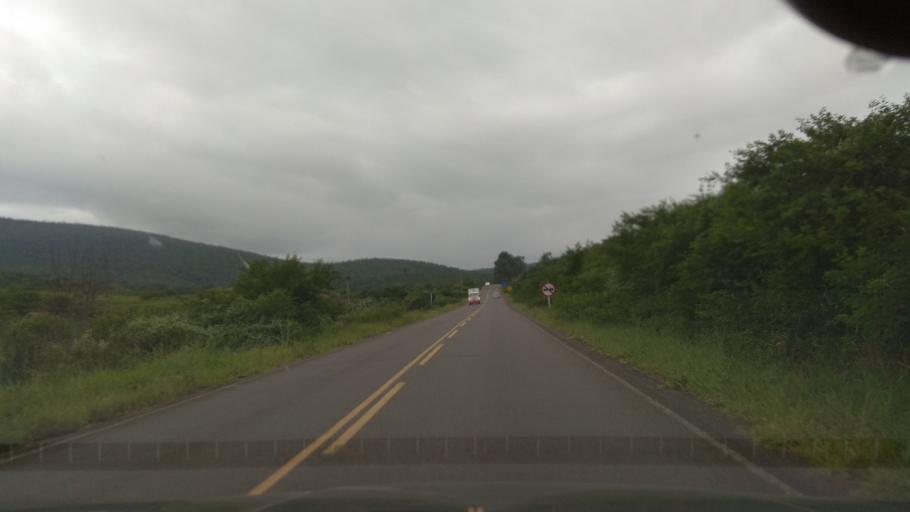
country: BR
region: Bahia
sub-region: Santa Ines
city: Santa Ines
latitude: -13.2751
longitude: -39.8096
